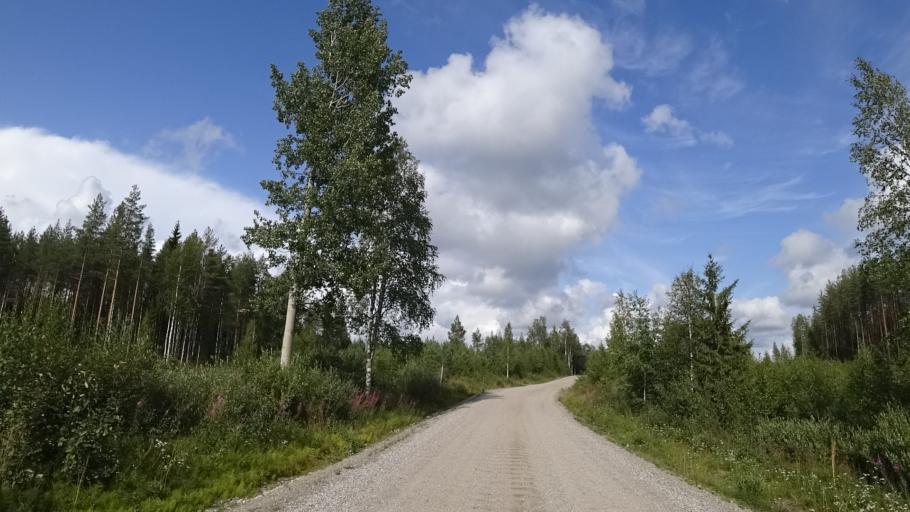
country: FI
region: North Karelia
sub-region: Pielisen Karjala
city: Lieksa
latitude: 63.5794
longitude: 30.1272
